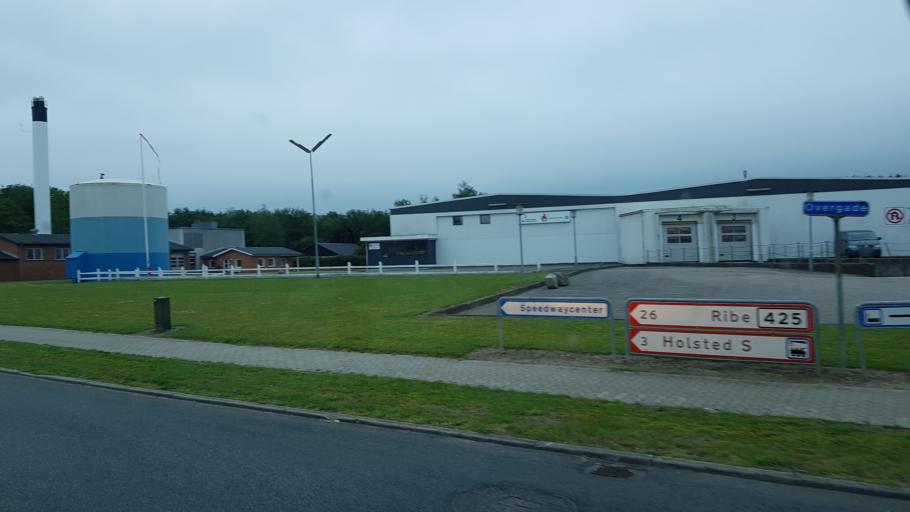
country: DK
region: South Denmark
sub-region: Vejen Kommune
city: Holsted
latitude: 55.5081
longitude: 8.9133
